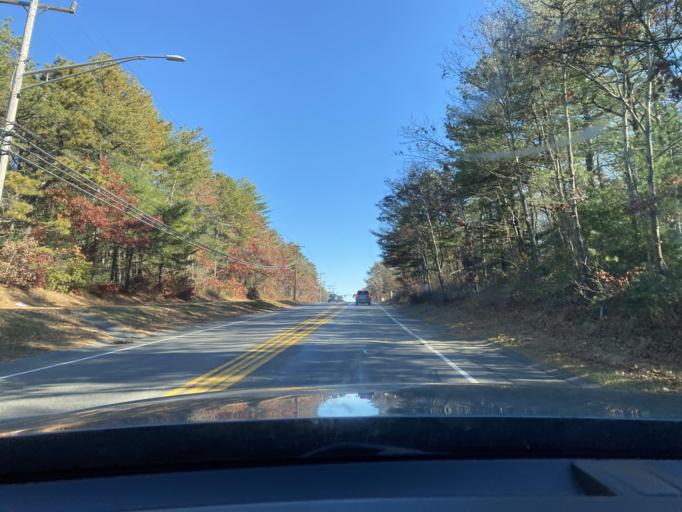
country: US
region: Massachusetts
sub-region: Barnstable County
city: Mashpee
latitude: 41.6178
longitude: -70.4984
